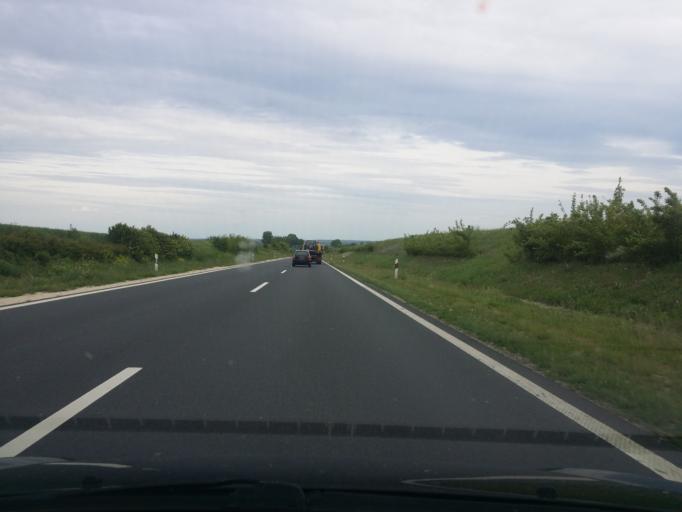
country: HU
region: Veszprem
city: Balatonkenese
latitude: 47.0288
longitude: 18.1739
